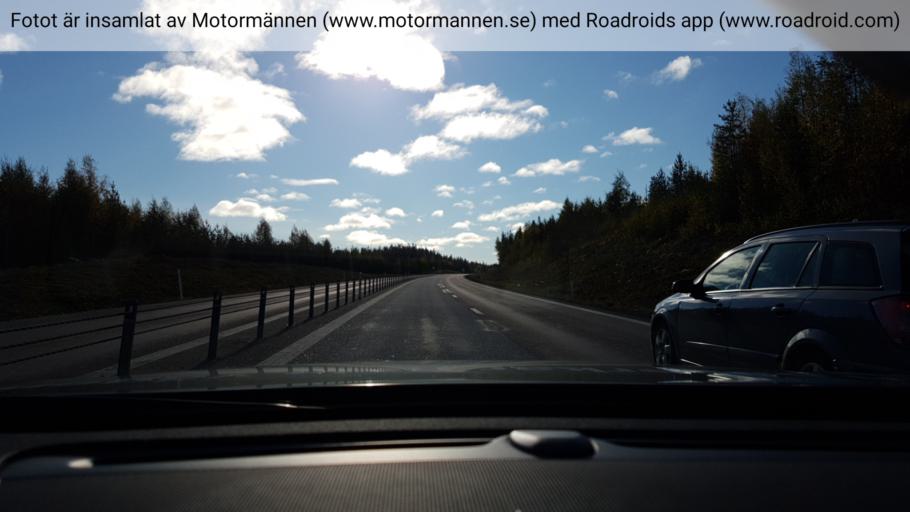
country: SE
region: Vaesterbotten
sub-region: Skelleftea Kommun
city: Skelleftea
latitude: 64.7161
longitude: 20.9915
